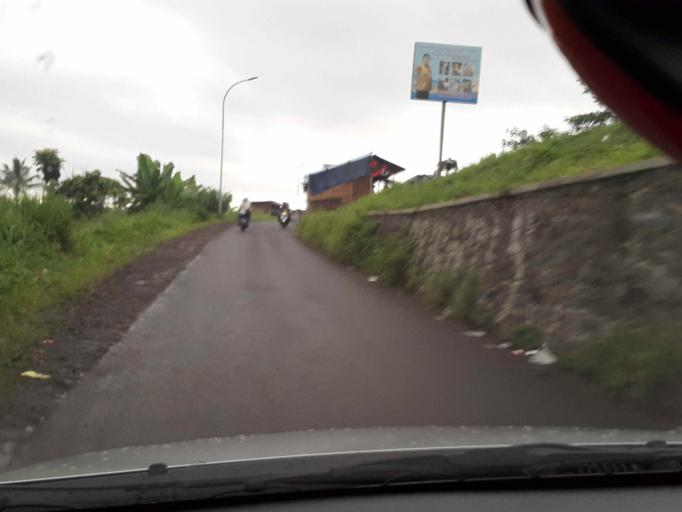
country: ID
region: West Java
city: Sukabumi
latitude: -6.9122
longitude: 106.8784
